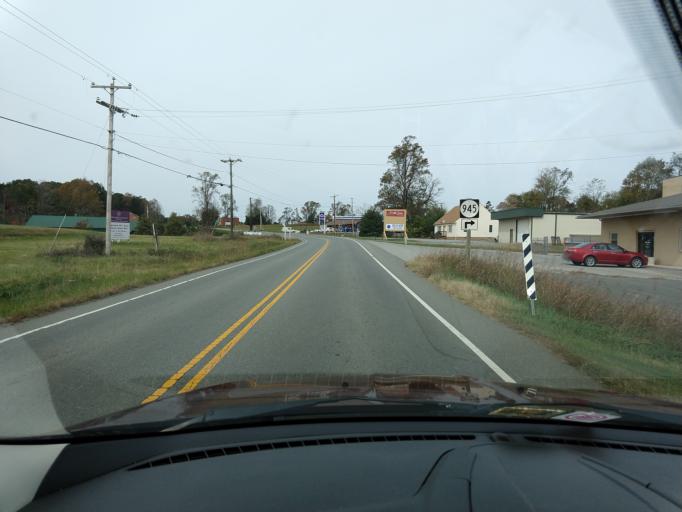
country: US
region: Virginia
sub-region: Franklin County
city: Union Hall
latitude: 36.9961
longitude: -79.6886
